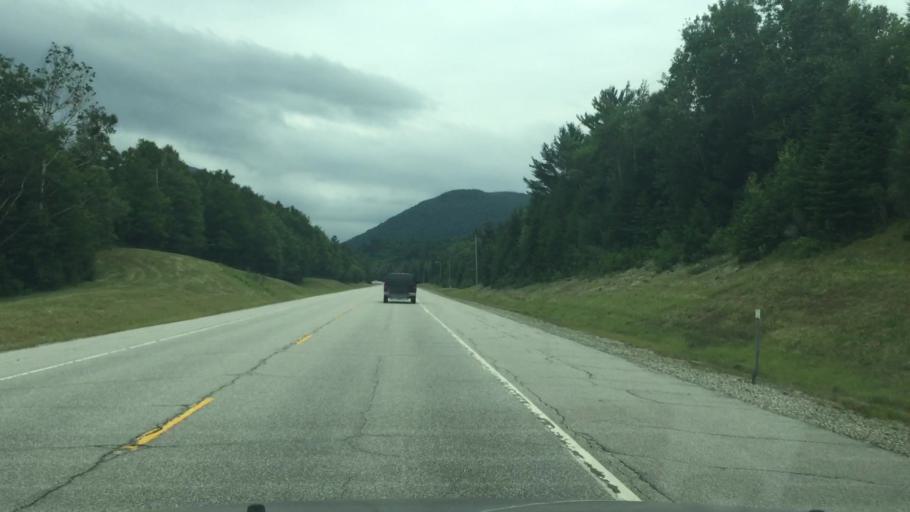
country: US
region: New Hampshire
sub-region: Coos County
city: Jefferson
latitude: 44.2332
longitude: -71.4215
